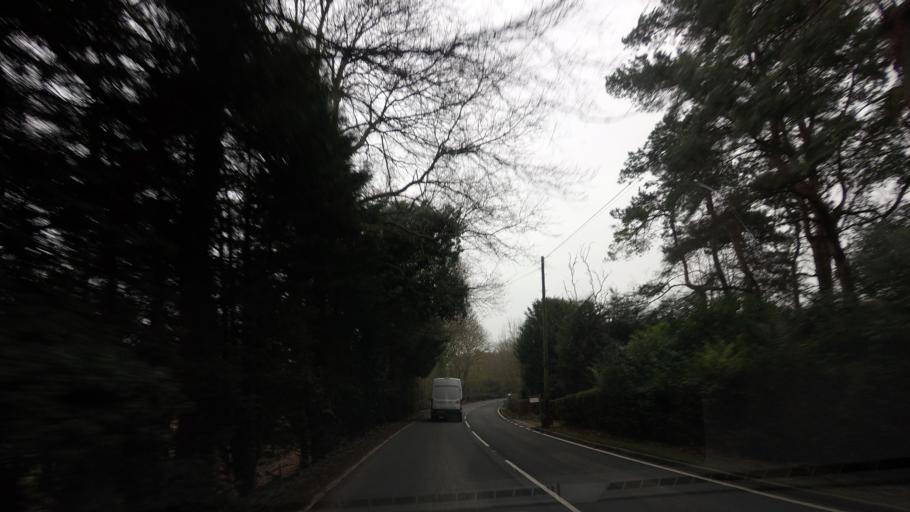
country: GB
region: England
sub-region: Kent
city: Cranbrook
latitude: 51.1227
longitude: 0.5585
